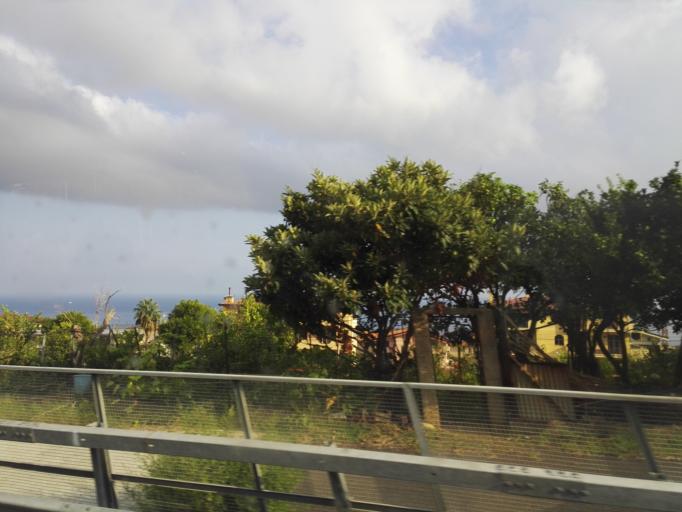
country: IT
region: Calabria
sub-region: Provincia di Reggio Calabria
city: Scilla
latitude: 38.2486
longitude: 15.7252
